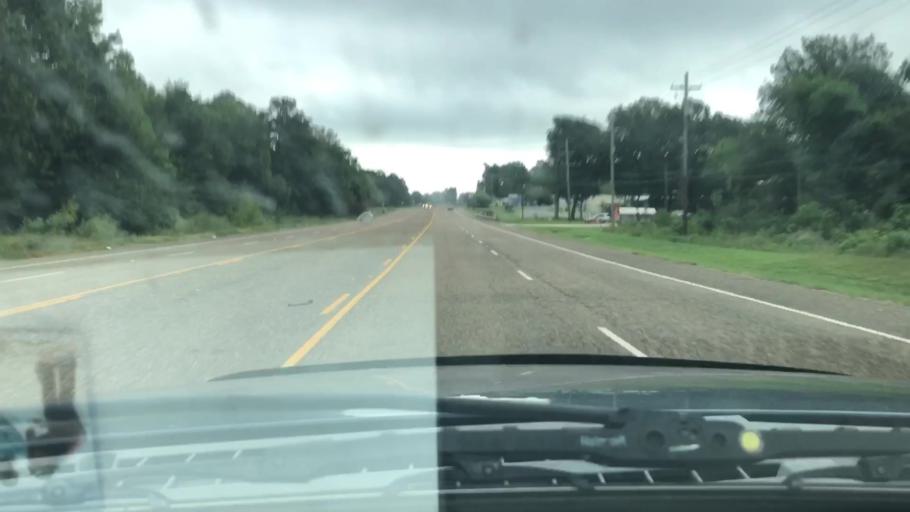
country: US
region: Texas
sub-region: Bowie County
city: Wake Village
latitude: 33.3974
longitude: -94.0897
